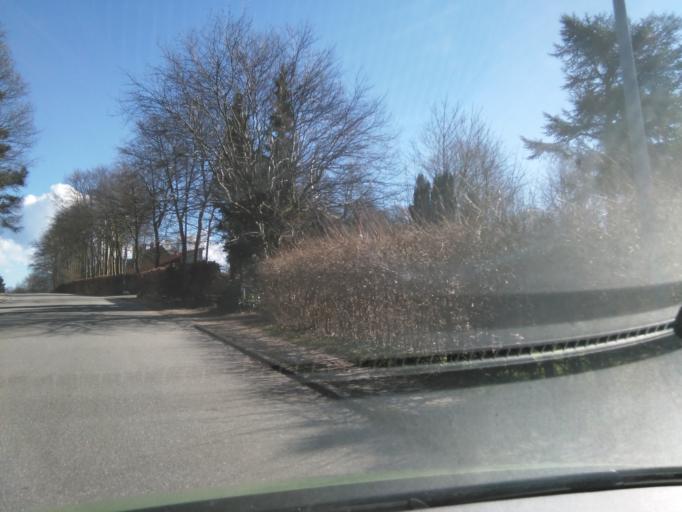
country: DK
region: Central Jutland
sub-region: Arhus Kommune
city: Arhus
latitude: 56.1097
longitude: 10.2186
